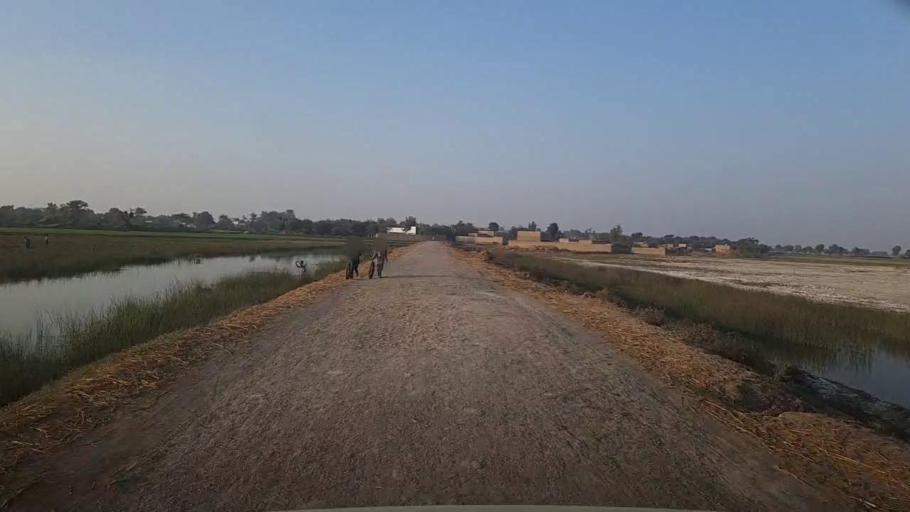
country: PK
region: Sindh
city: Mehar
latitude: 27.1961
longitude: 67.7820
